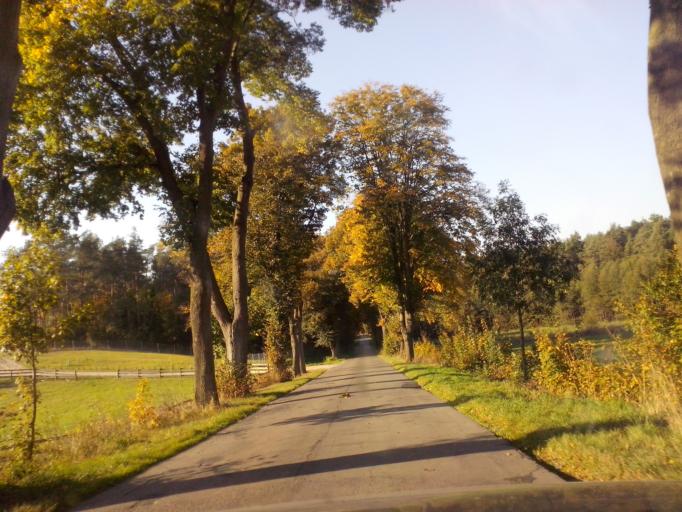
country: PL
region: Kujawsko-Pomorskie
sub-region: Powiat brodnicki
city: Bartniczka
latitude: 53.2347
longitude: 19.6261
